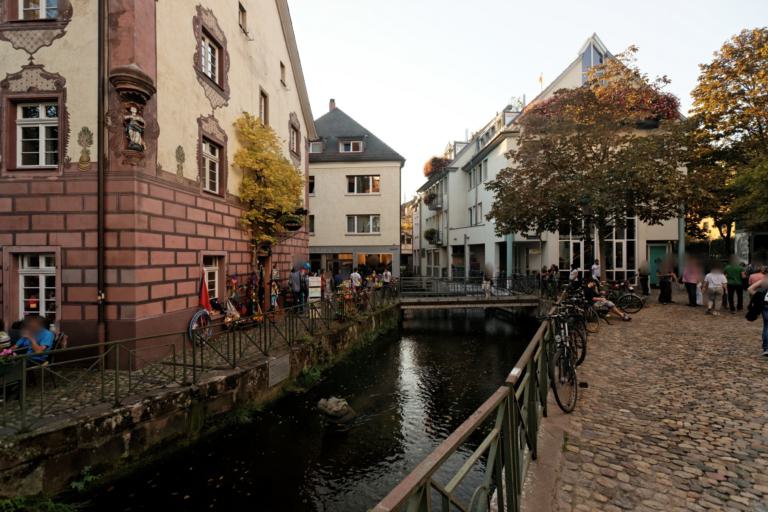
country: DE
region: Baden-Wuerttemberg
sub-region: Freiburg Region
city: Freiburg
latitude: 47.9931
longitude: 7.8531
